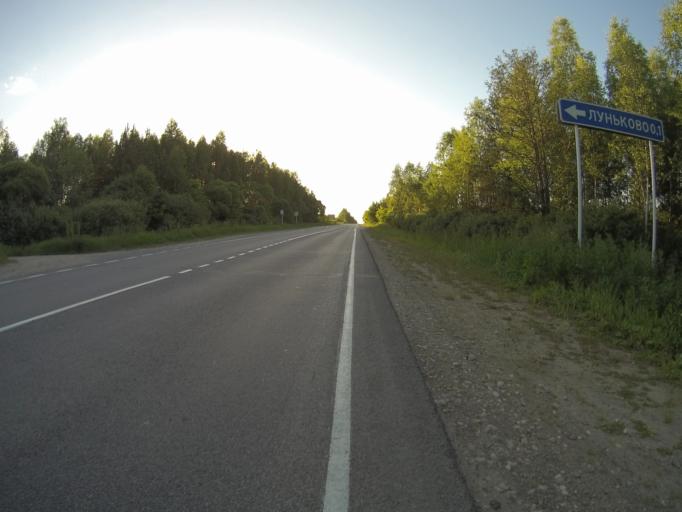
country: RU
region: Vladimir
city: Golovino
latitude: 55.9535
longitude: 40.5708
